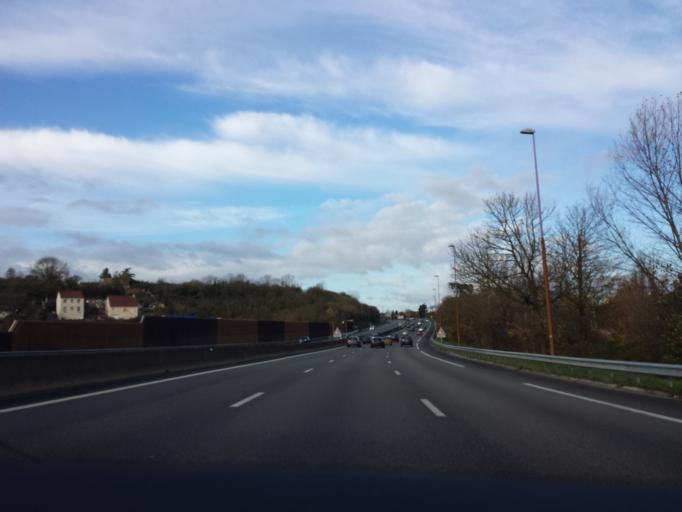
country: FR
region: Ile-de-France
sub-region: Departement des Yvelines
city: Mantes-la-Jolie
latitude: 48.9709
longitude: 1.7332
